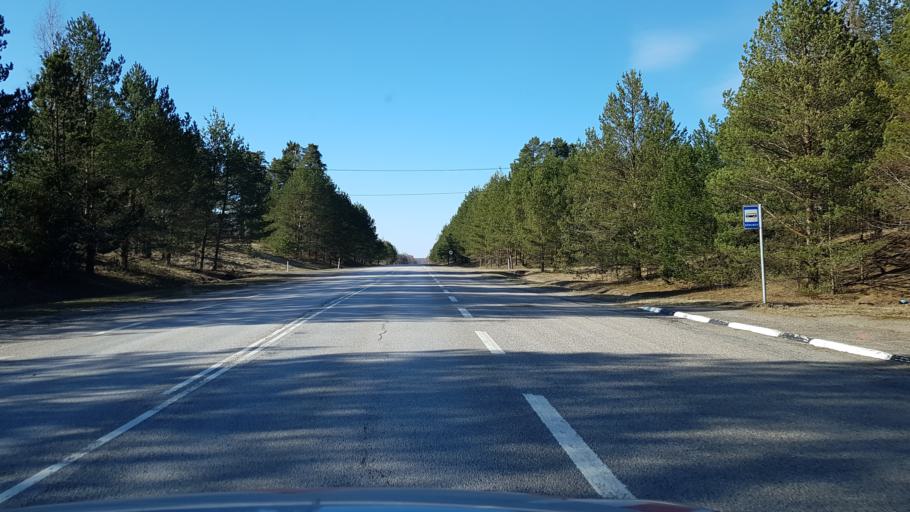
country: EE
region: Ida-Virumaa
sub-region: Johvi vald
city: Johvi
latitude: 59.1642
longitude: 27.3530
